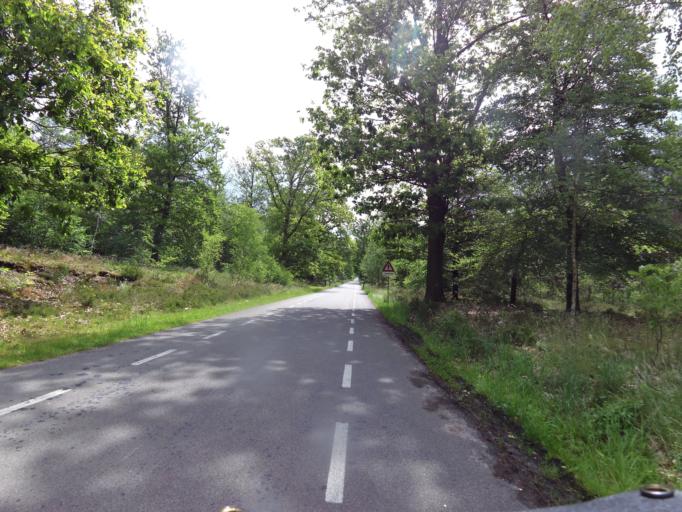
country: NL
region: Gelderland
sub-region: Gemeente Epe
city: Vaassen
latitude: 52.3080
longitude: 5.8959
